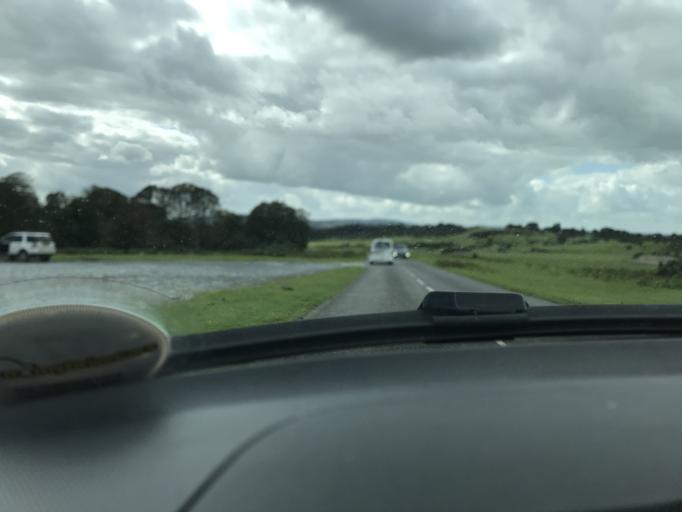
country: GB
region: England
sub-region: Devon
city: Tavistock
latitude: 50.5424
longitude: -4.1116
